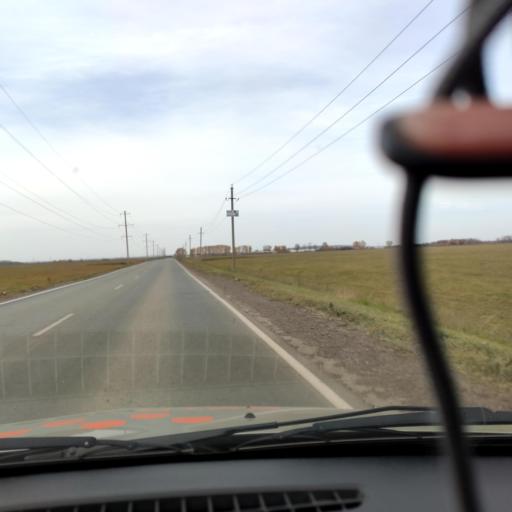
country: RU
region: Bashkortostan
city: Kabakovo
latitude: 54.5394
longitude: 56.0623
